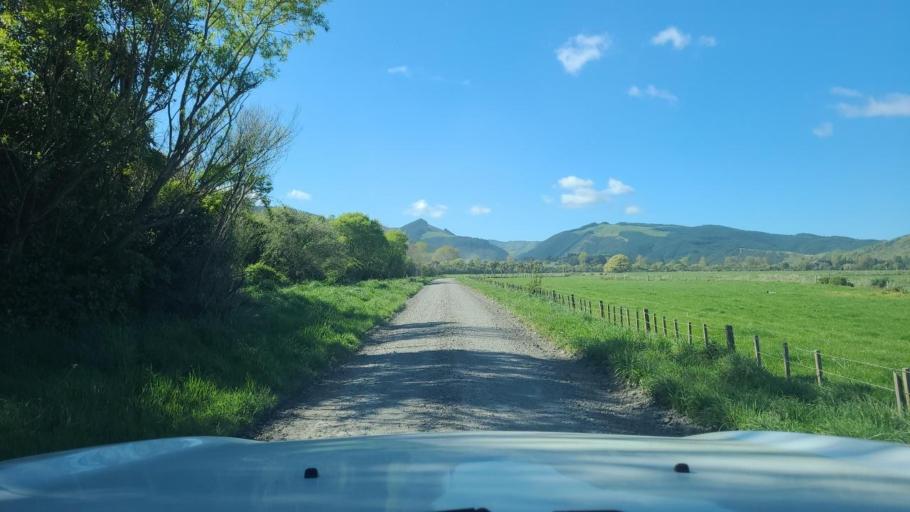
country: NZ
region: Wellington
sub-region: Upper Hutt City
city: Upper Hutt
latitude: -41.3809
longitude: 175.2150
